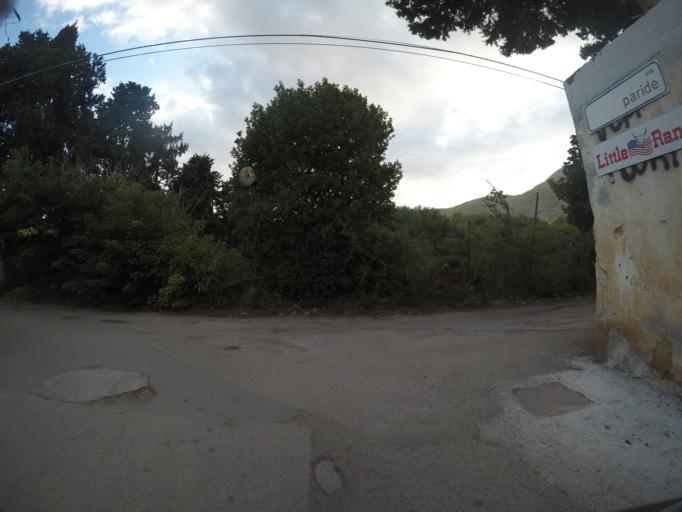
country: IT
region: Sicily
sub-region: Palermo
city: Isola delle Femmine
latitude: 38.2002
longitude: 13.3101
